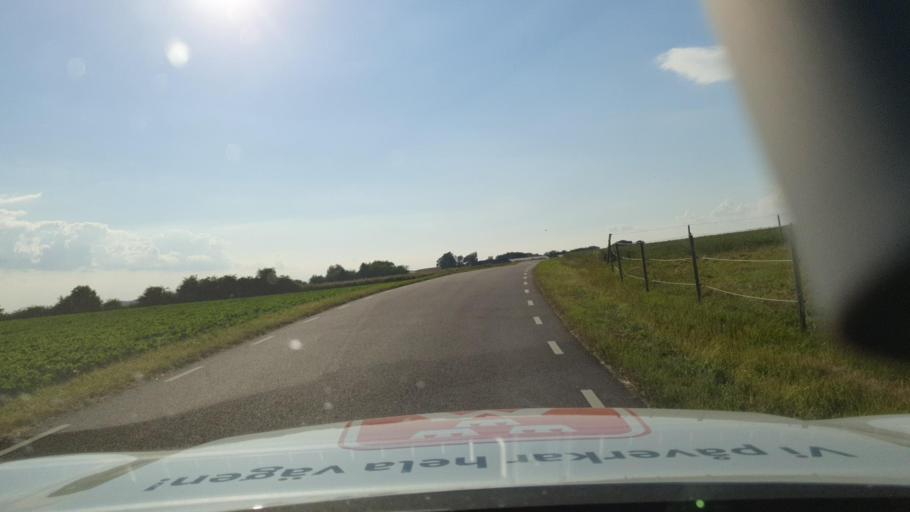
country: SE
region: Skane
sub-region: Skurups Kommun
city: Rydsgard
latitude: 55.5037
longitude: 13.5722
